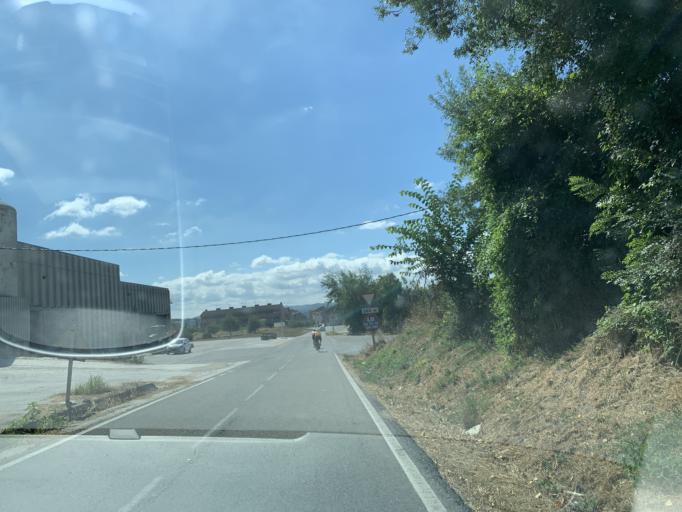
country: ES
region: Catalonia
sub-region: Provincia de Tarragona
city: Santa Coloma de Queralt
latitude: 41.5382
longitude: 1.3781
